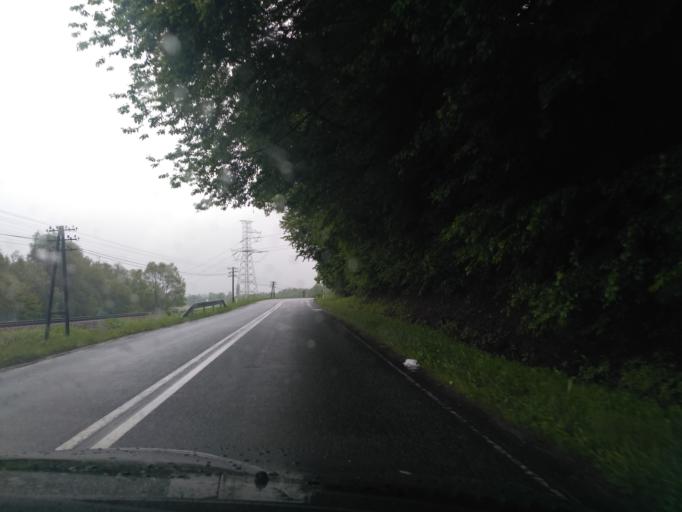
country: PL
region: Subcarpathian Voivodeship
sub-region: Powiat krosnienski
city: Leki
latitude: 49.8077
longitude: 21.6388
